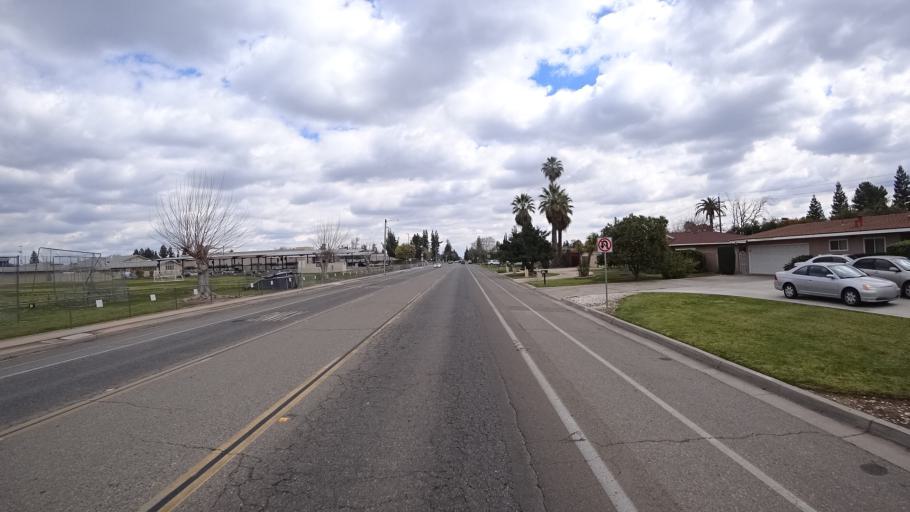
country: US
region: California
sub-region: Fresno County
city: Fresno
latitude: 36.8156
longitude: -119.8123
